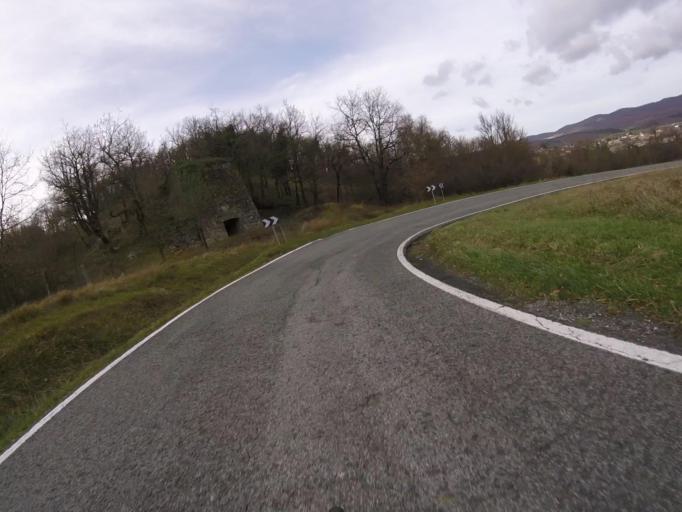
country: ES
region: Navarre
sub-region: Provincia de Navarra
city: Olazagutia
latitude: 42.8812
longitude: -2.1795
